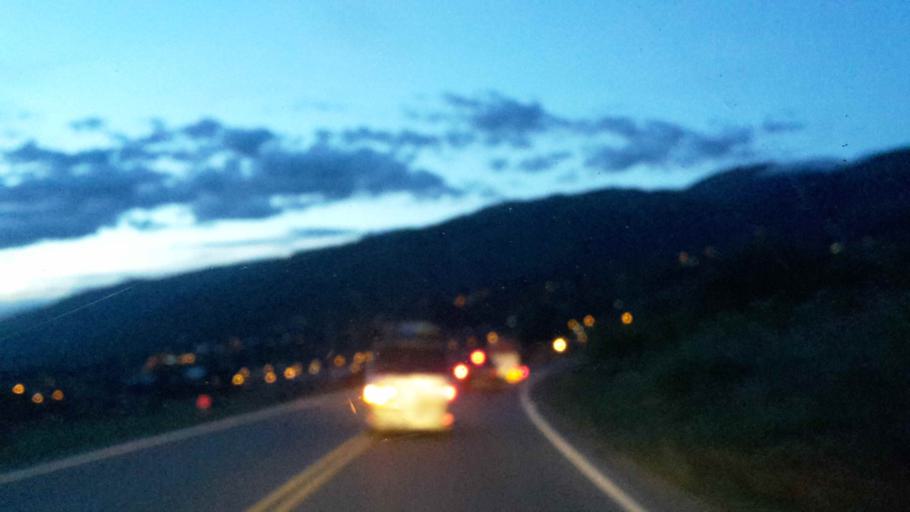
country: BO
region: Cochabamba
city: Colomi
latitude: -17.4087
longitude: -65.9689
